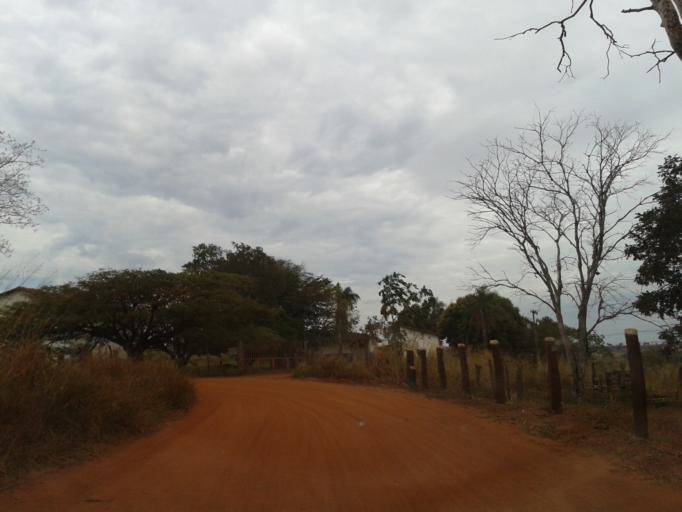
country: BR
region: Minas Gerais
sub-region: Santa Vitoria
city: Santa Vitoria
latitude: -18.8493
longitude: -50.1084
